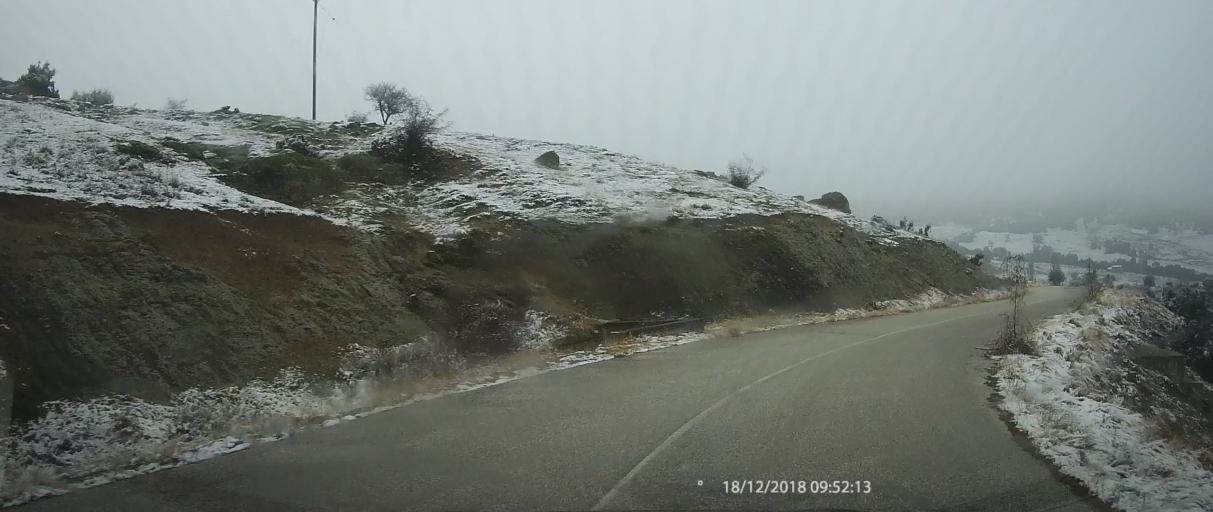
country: GR
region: Thessaly
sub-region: Nomos Larisis
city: Livadi
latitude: 40.0283
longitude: 22.2514
